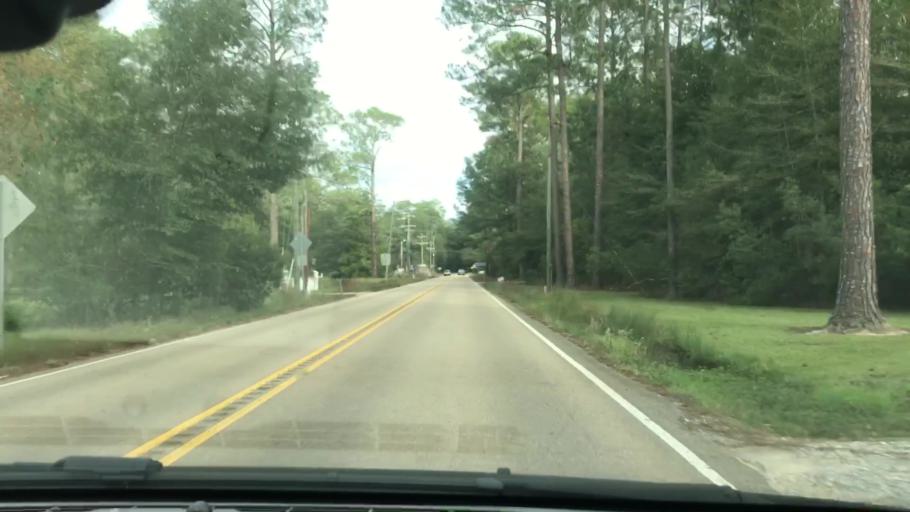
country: US
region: Louisiana
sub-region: Saint Tammany Parish
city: Abita Springs
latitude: 30.4900
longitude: -90.0211
